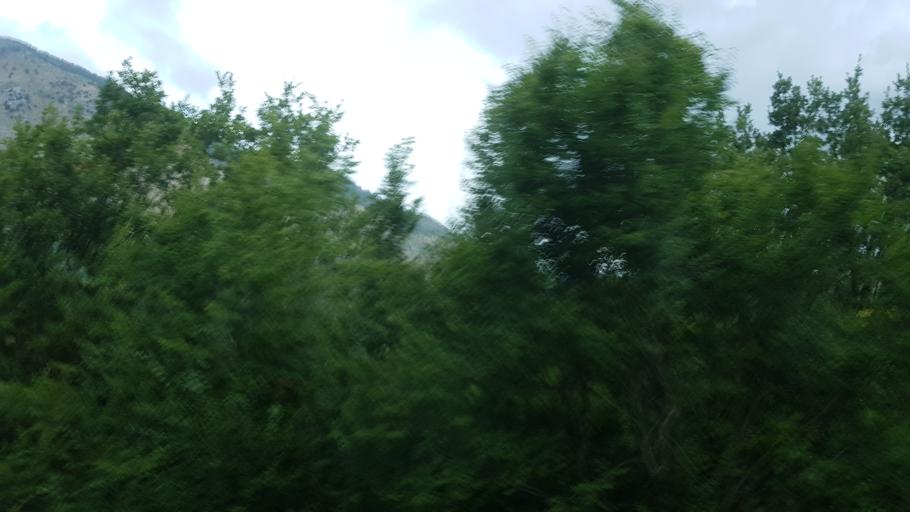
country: AL
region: Vlore
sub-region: Rrethi i Sarandes
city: Dhiver
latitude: 39.9160
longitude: 20.1920
